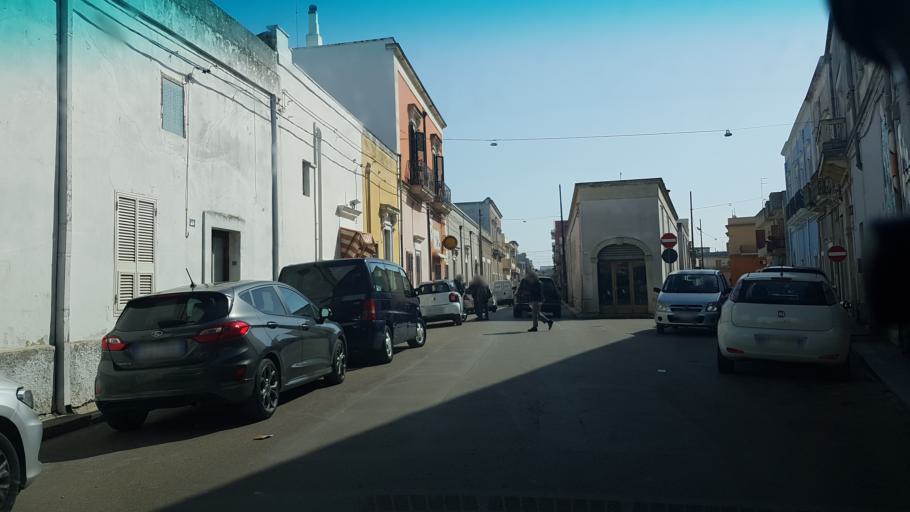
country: IT
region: Apulia
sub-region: Provincia di Brindisi
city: San Pietro Vernotico
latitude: 40.4867
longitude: 17.9989
